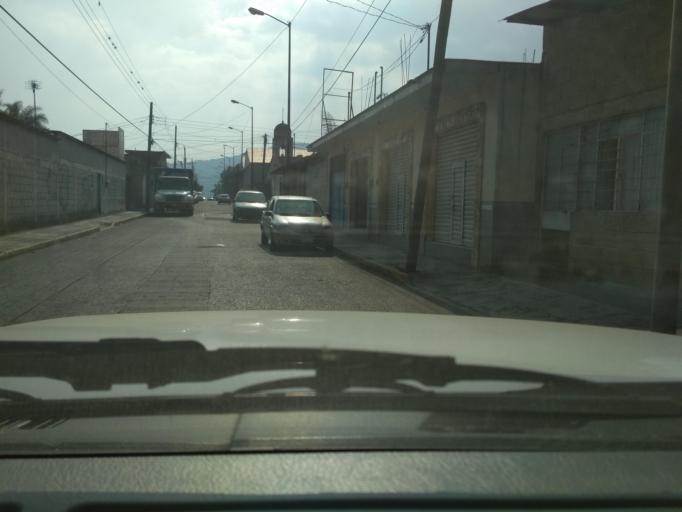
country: MX
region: Veracruz
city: Orizaba
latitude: 18.8694
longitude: -97.0944
